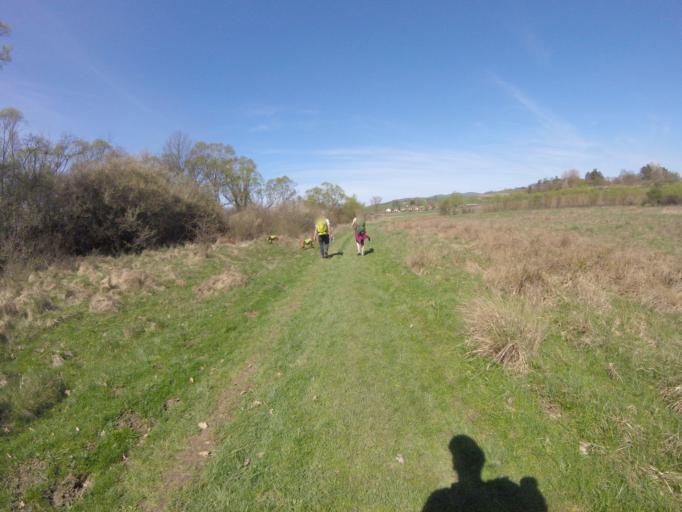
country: HU
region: Borsod-Abauj-Zemplen
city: Szendro
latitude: 48.4130
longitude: 20.7769
